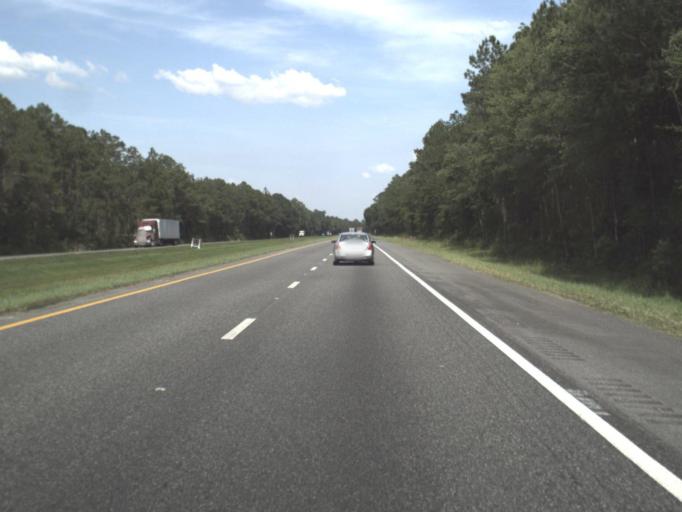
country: US
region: Florida
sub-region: Columbia County
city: Watertown
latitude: 30.2470
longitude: -82.5517
